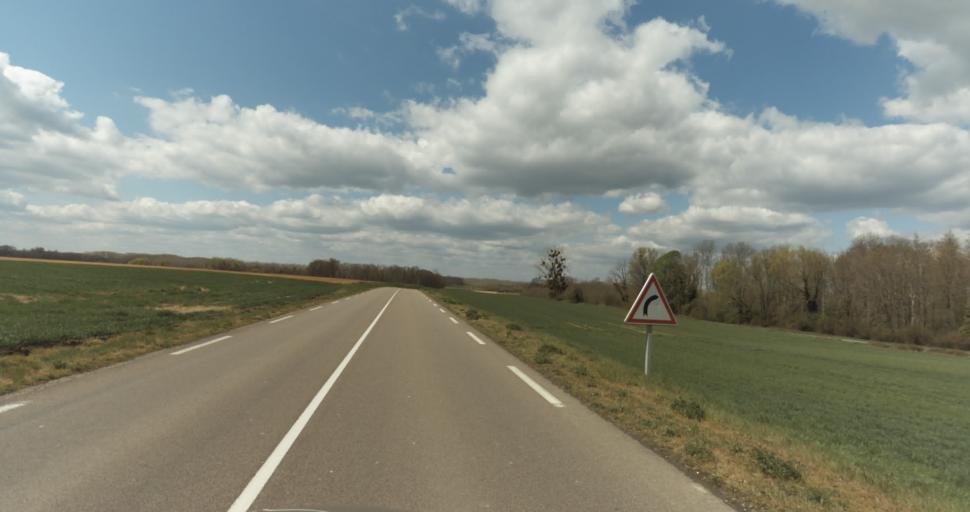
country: FR
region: Bourgogne
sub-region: Departement de la Cote-d'Or
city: Auxonne
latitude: 47.1620
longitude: 5.4072
